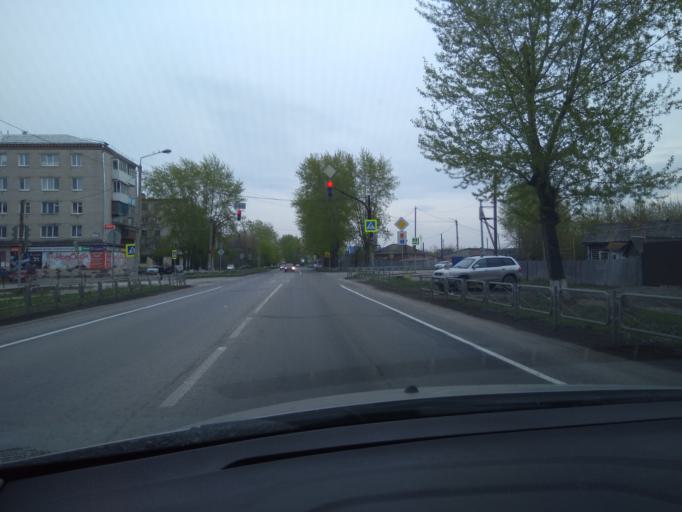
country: RU
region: Sverdlovsk
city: Bogdanovich
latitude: 56.7709
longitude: 62.0443
